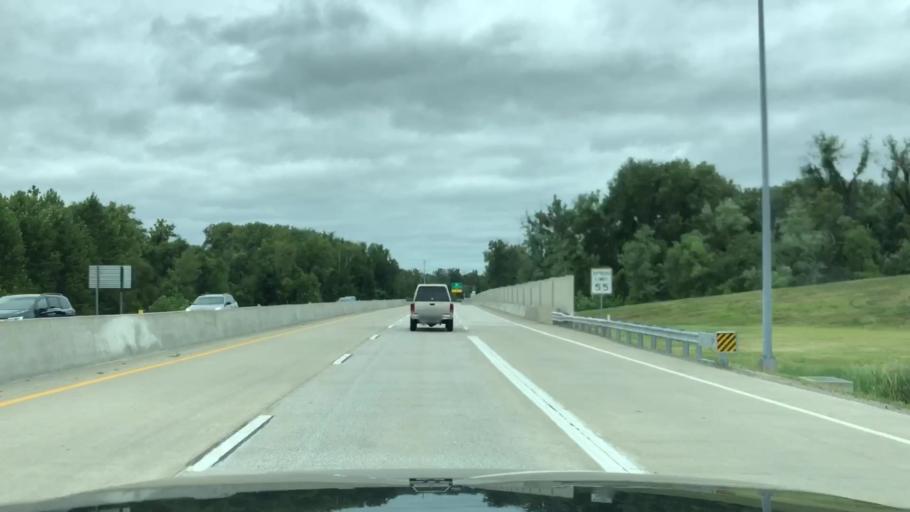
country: US
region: Missouri
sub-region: Saint Louis County
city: Town and Country
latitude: 38.6775
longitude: -90.4935
